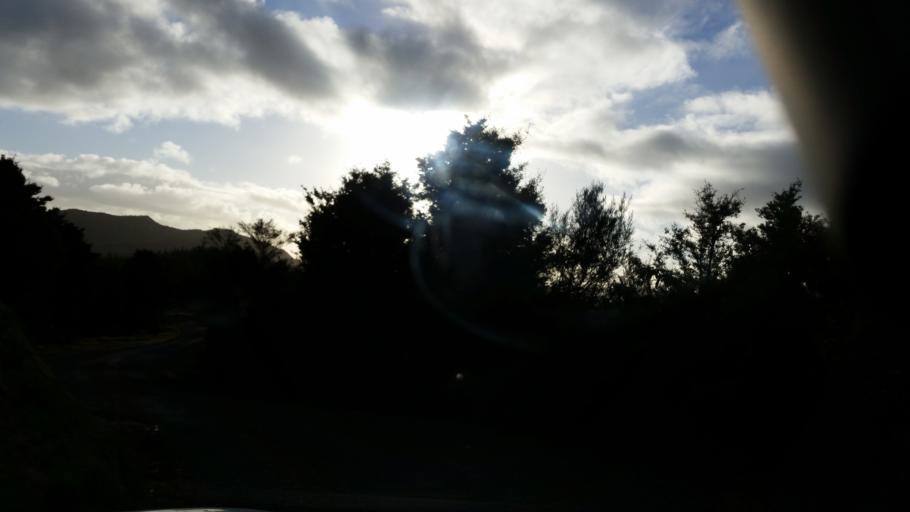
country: NZ
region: Northland
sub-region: Whangarei
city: Maungatapere
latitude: -35.7870
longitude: 174.0810
